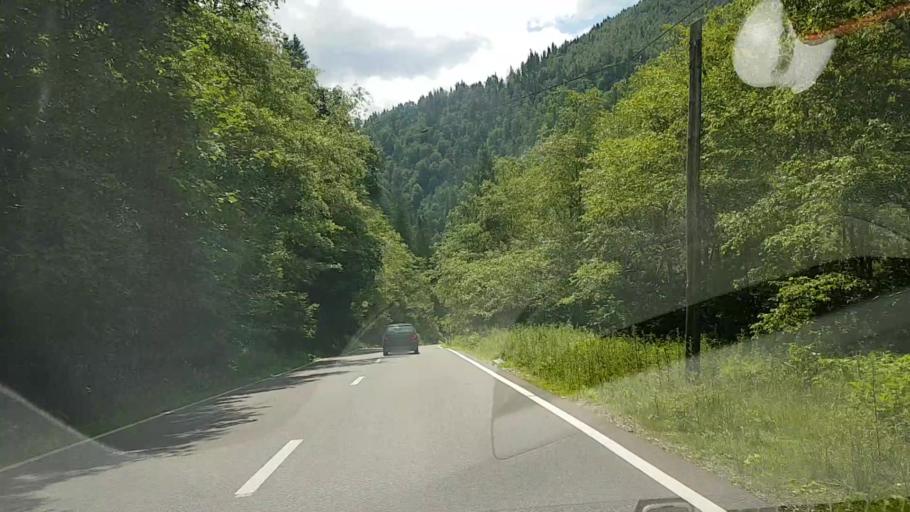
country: RO
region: Suceava
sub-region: Comuna Brosteni
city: Brosteni
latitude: 47.2780
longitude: 25.6497
